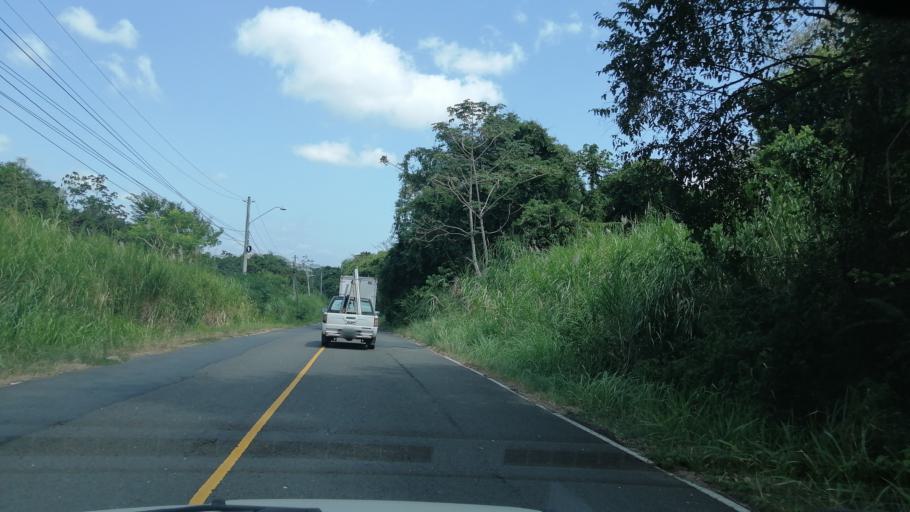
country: PA
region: Panama
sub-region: Distrito de Panama
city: Ancon
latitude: 8.9227
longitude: -79.5657
